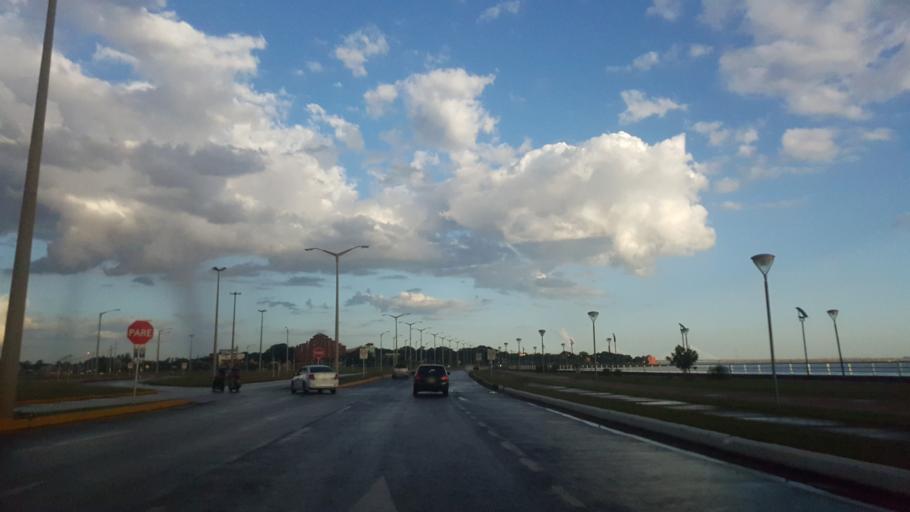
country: PY
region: Itapua
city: Encarnacion
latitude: -27.3430
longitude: -55.8705
